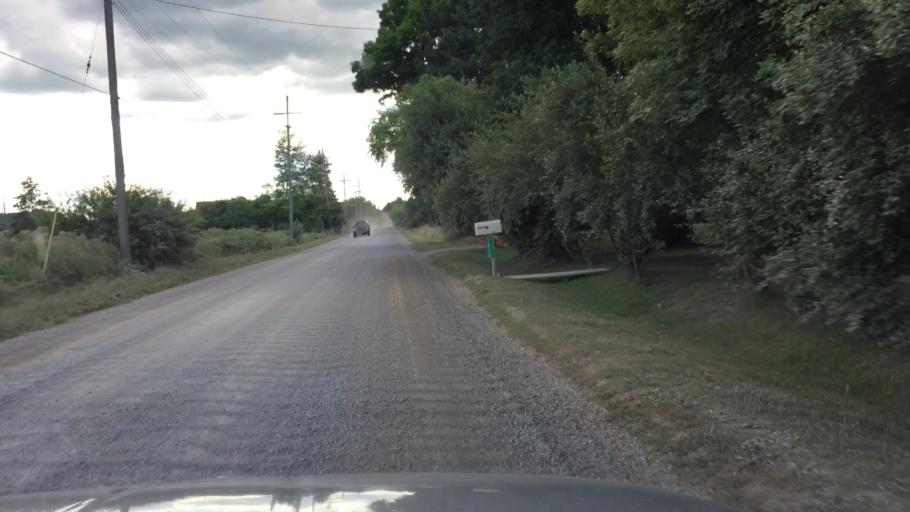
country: US
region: Michigan
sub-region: Saint Clair County
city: Yale
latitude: 43.1443
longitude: -82.8076
